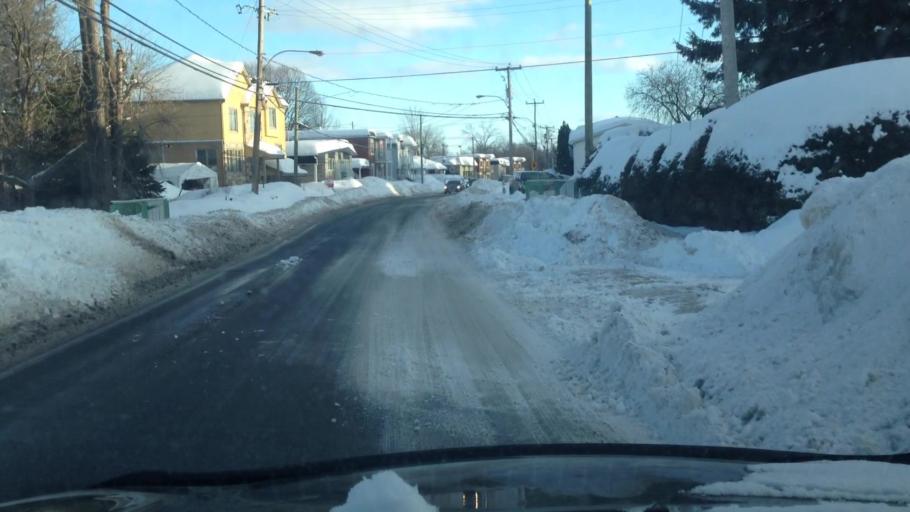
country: CA
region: Quebec
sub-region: Laurentides
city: Saint-Jerome
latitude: 45.7957
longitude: -74.0142
